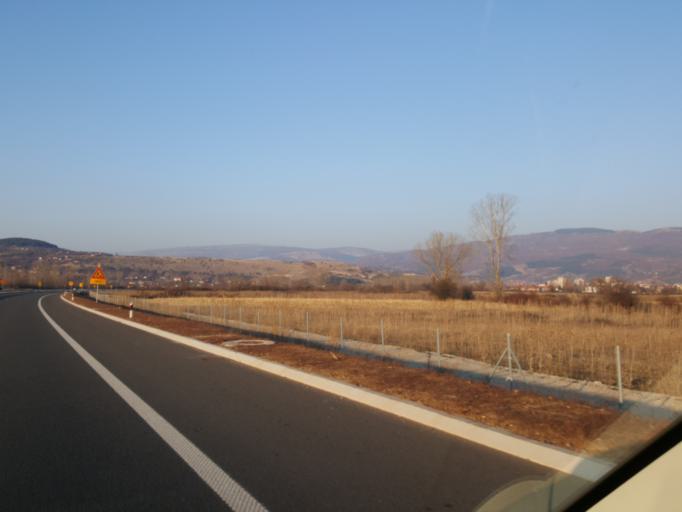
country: RS
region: Central Serbia
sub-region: Pirotski Okrug
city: Pirot
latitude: 43.1433
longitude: 22.5677
